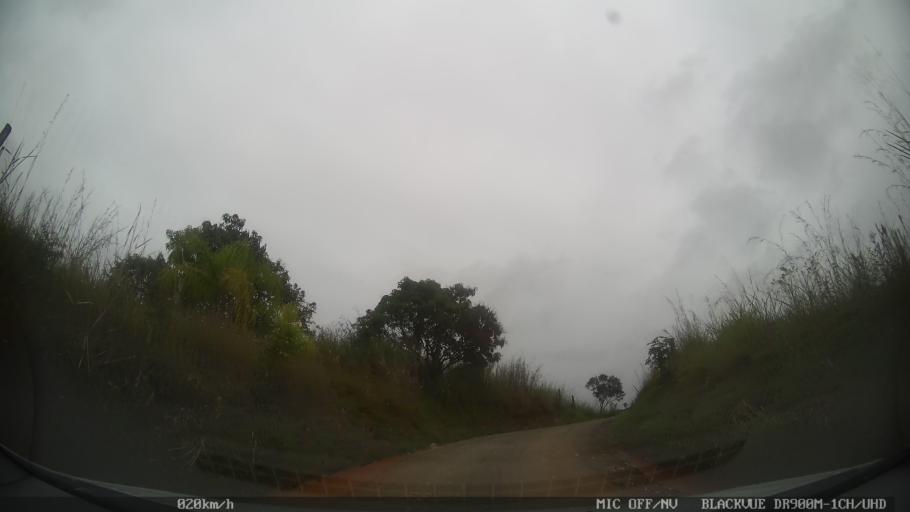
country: BR
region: Sao Paulo
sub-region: Cajati
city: Cajati
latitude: -24.7890
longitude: -48.1819
